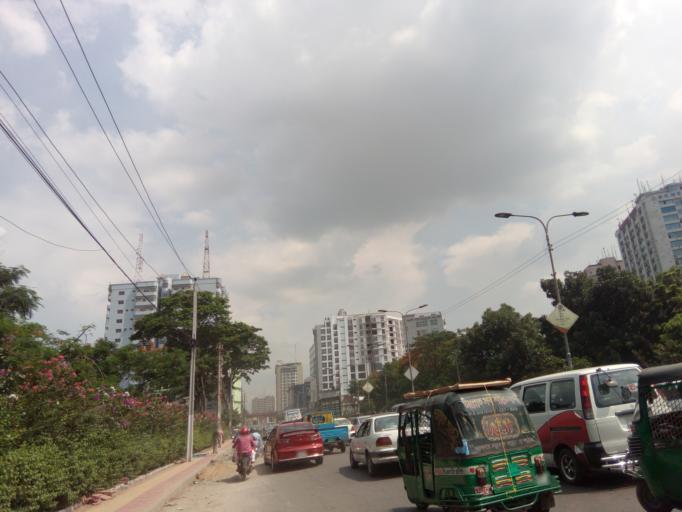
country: BD
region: Dhaka
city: Azimpur
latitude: 23.7485
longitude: 90.3940
